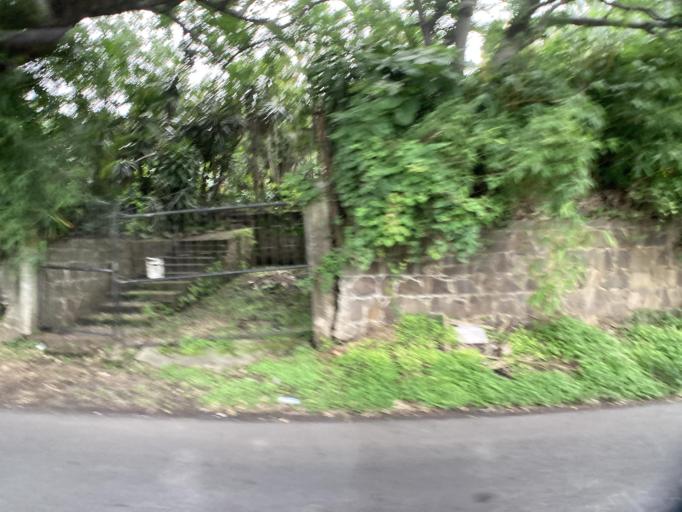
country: GT
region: Guatemala
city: Villa Canales
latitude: 14.4386
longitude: -90.5359
